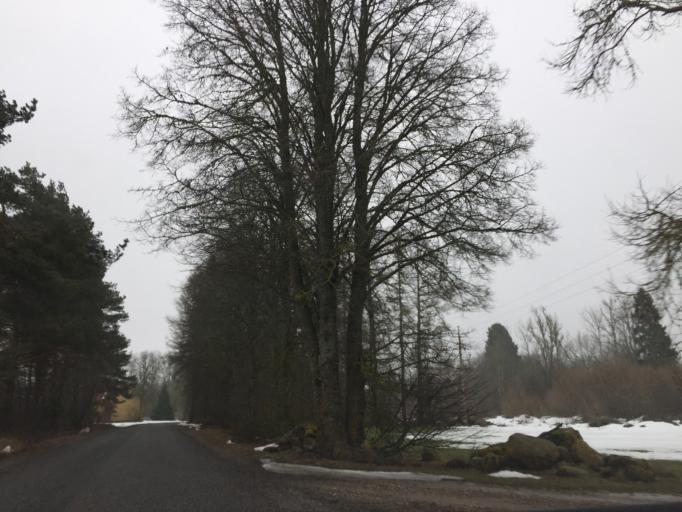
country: EE
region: Saare
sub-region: Kuressaare linn
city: Kuressaare
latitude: 58.2715
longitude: 22.5810
